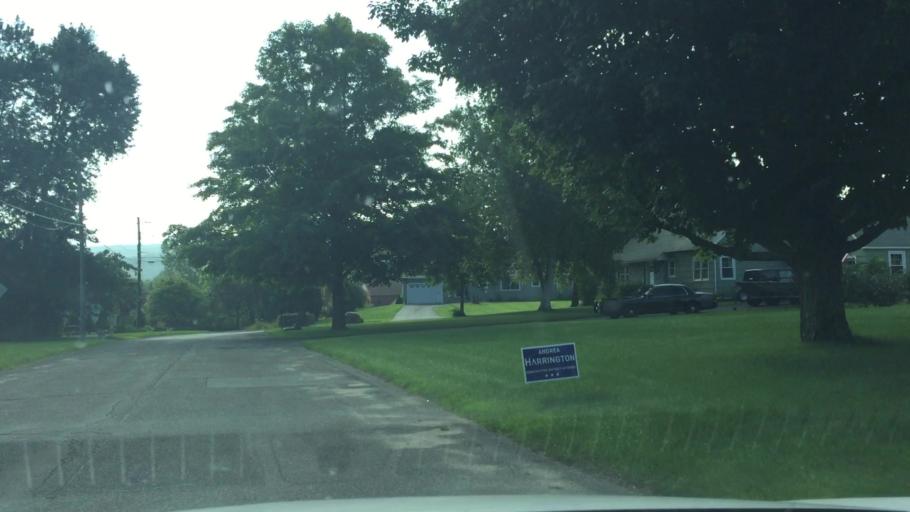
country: US
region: Massachusetts
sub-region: Berkshire County
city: Pittsfield
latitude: 42.4293
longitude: -73.2098
